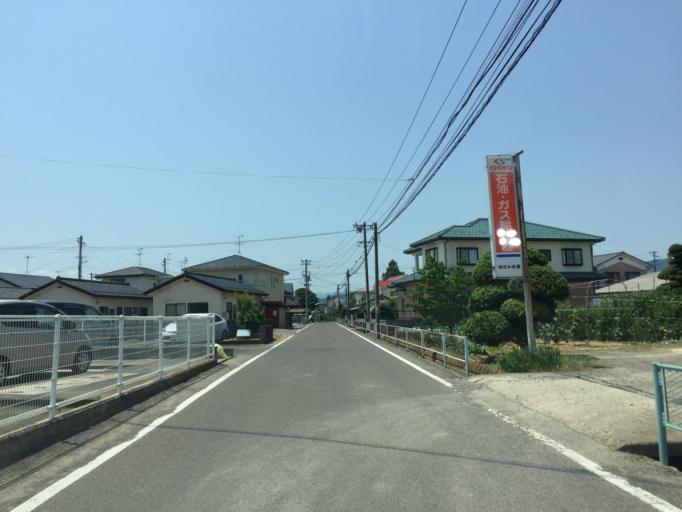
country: JP
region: Fukushima
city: Hobaramachi
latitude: 37.8264
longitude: 140.5521
